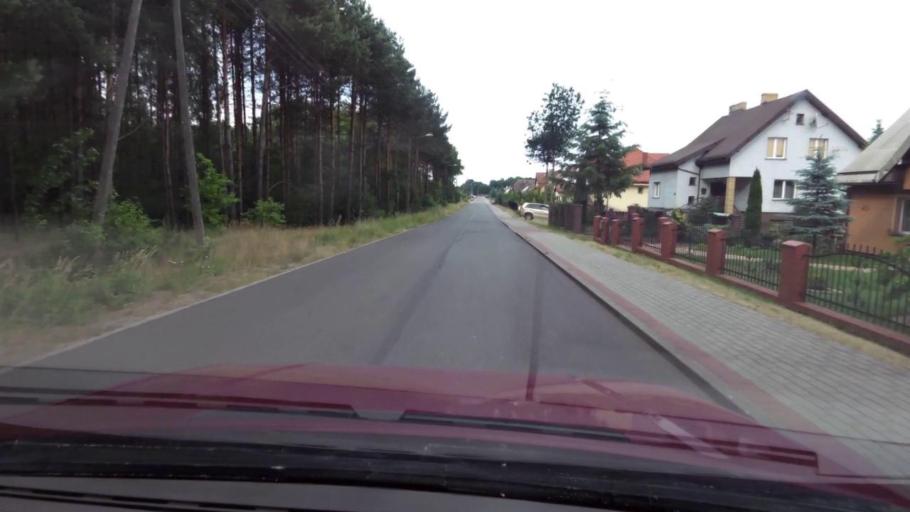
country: PL
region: Pomeranian Voivodeship
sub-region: Powiat bytowski
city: Trzebielino
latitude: 54.1984
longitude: 17.0747
